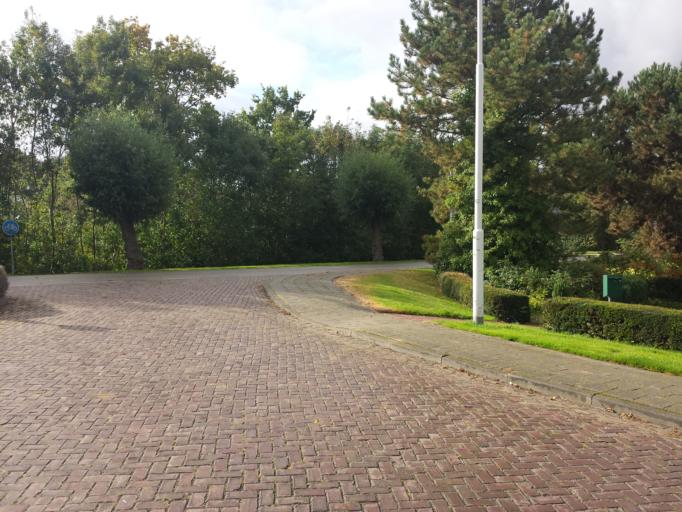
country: NL
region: Zeeland
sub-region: Gemeente Vlissingen
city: Vlissingen
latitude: 51.3922
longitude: 3.5546
